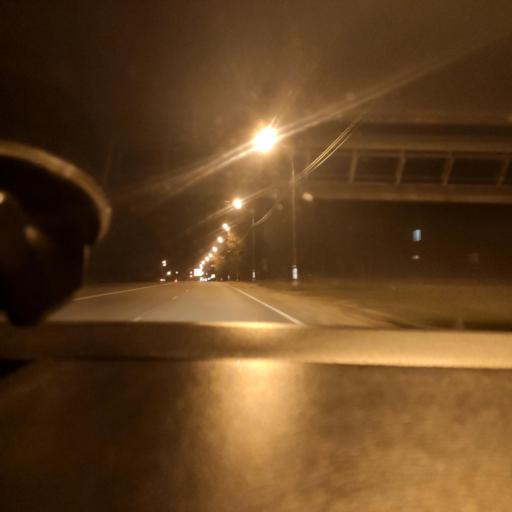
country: RU
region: Moskovskaya
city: Beloozerskiy
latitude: 55.3712
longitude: 38.3876
